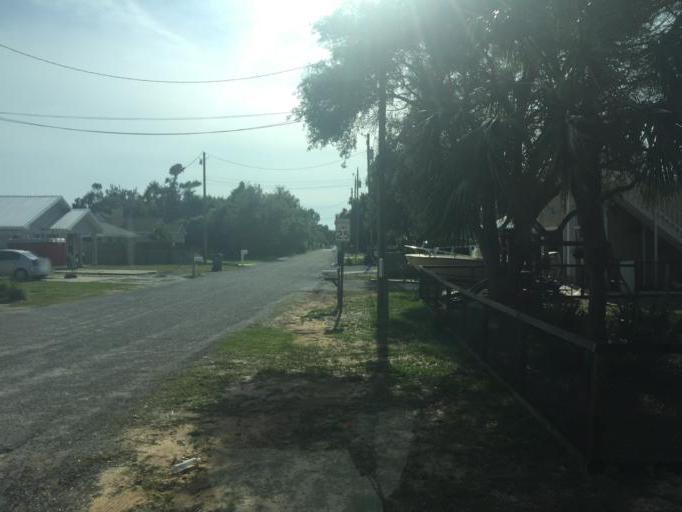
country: US
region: Florida
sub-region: Bay County
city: Laguna Beach
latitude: 30.2560
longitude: -85.9502
